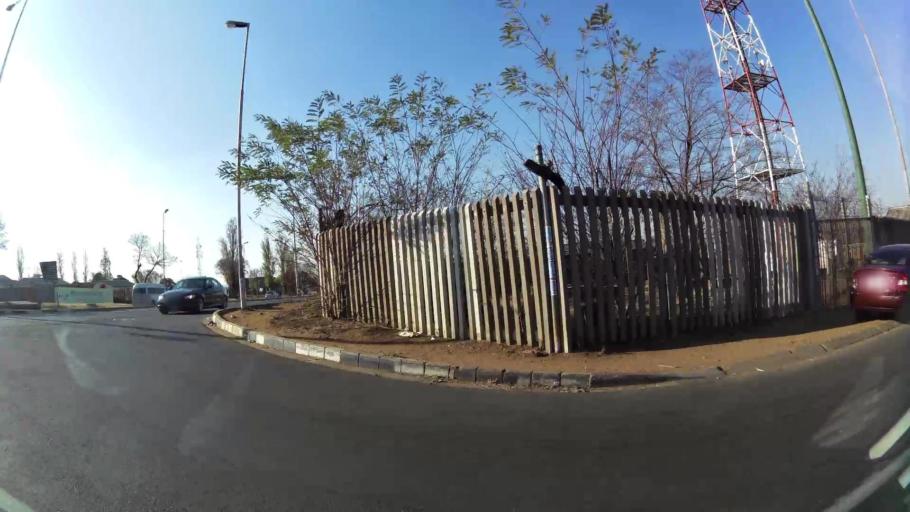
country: ZA
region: Gauteng
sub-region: City of Johannesburg Metropolitan Municipality
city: Soweto
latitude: -26.2705
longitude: 27.8751
